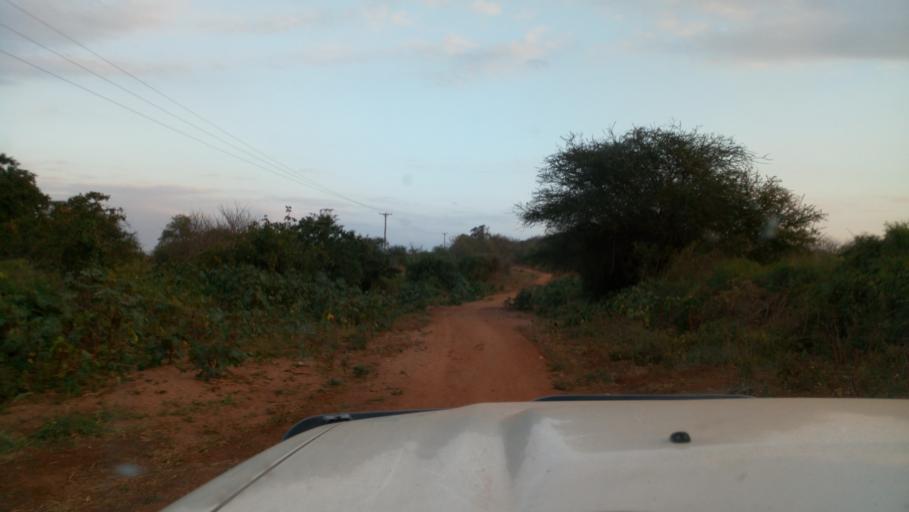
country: KE
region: Kitui
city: Kitui
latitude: -1.7036
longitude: 38.2434
